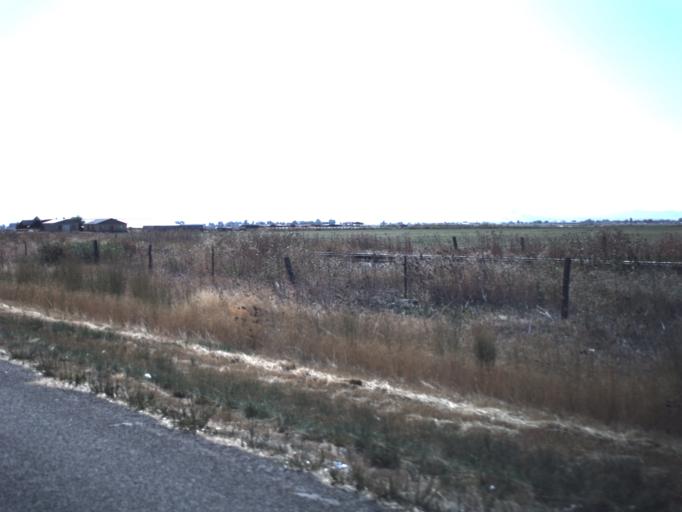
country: US
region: Utah
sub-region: Cache County
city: Lewiston
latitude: 41.9966
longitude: -111.8129
